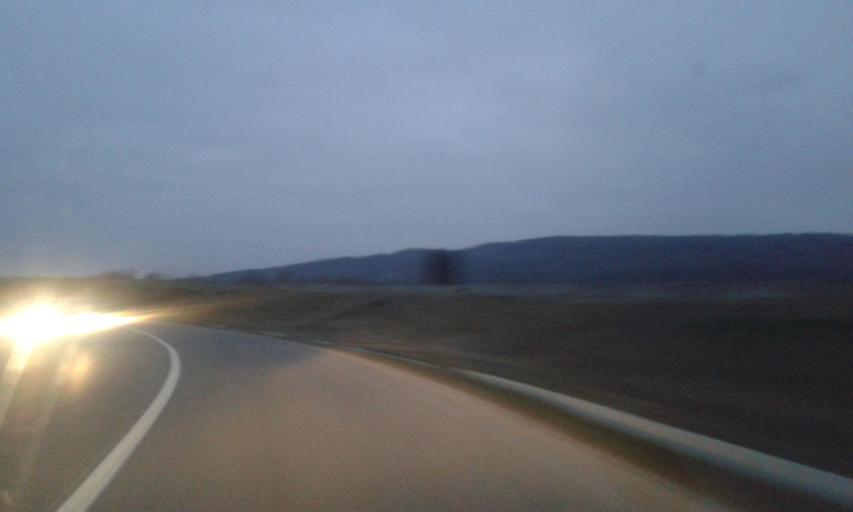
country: RO
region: Gorj
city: Targu Jiu
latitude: 45.0711
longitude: 23.2853
